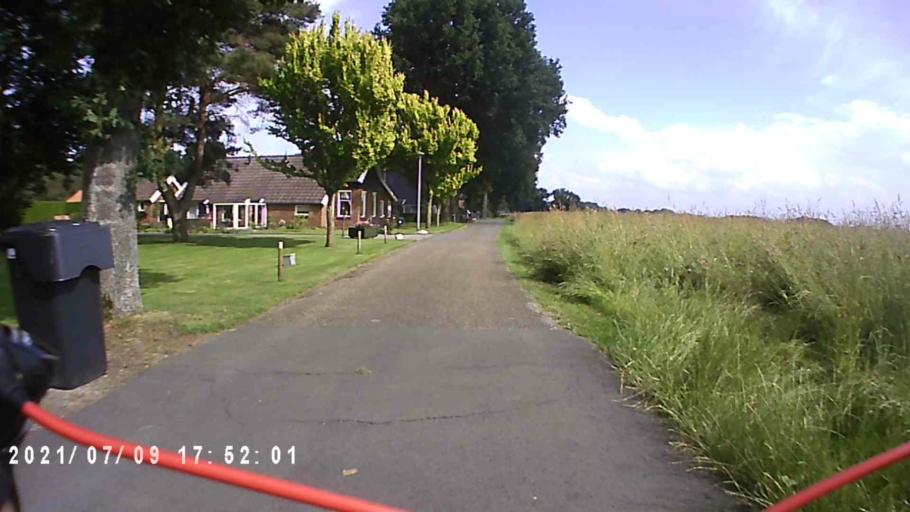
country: NL
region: Groningen
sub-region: Gemeente Vlagtwedde
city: Vlagtwedde
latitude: 53.0676
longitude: 7.0769
